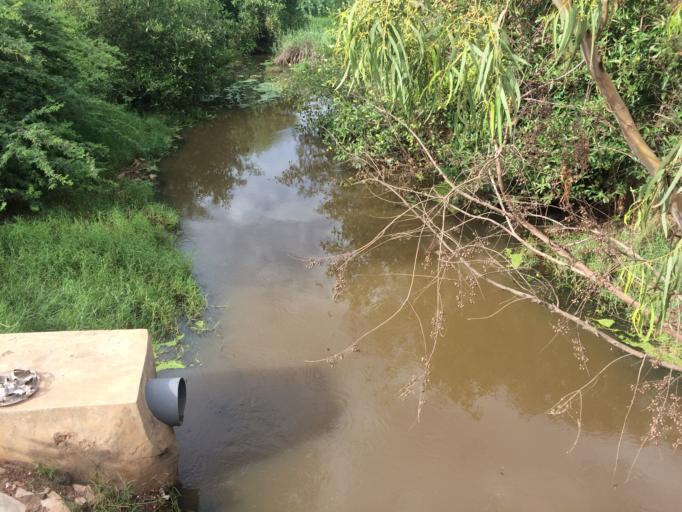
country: SN
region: Dakar
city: Pikine
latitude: 14.7474
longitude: -17.3236
